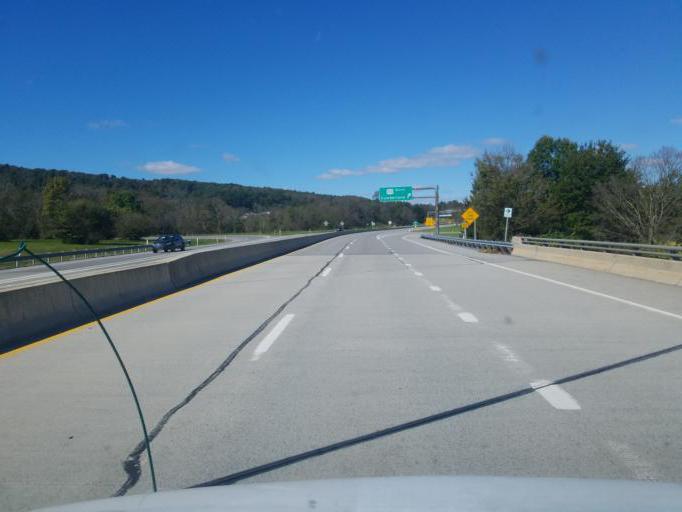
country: US
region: Pennsylvania
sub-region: Bedford County
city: Bedford
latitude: 40.0262
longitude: -78.5137
